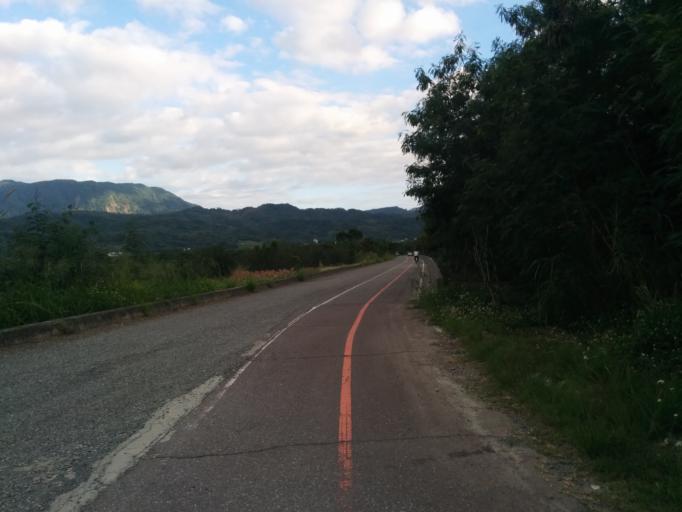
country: TW
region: Taiwan
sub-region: Taitung
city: Taitung
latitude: 23.0271
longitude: 121.1590
